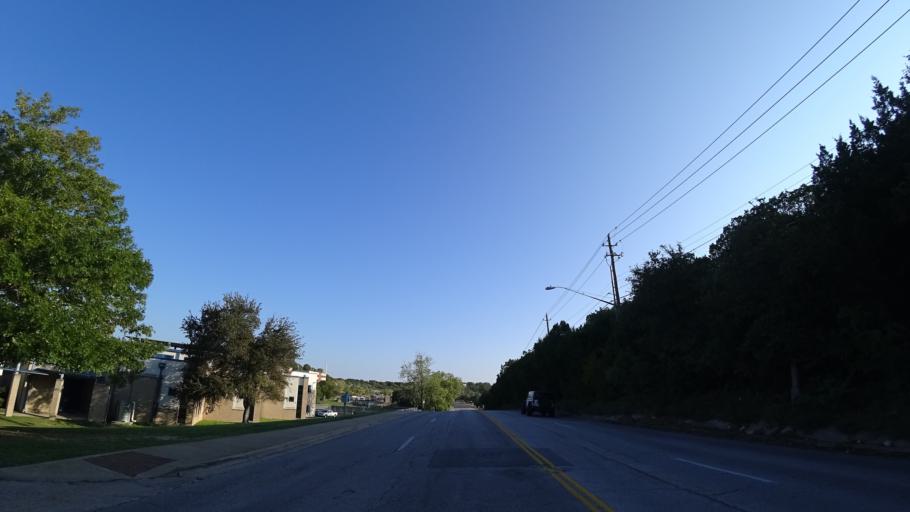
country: US
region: Texas
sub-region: Travis County
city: Rollingwood
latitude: 30.2707
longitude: -97.8028
